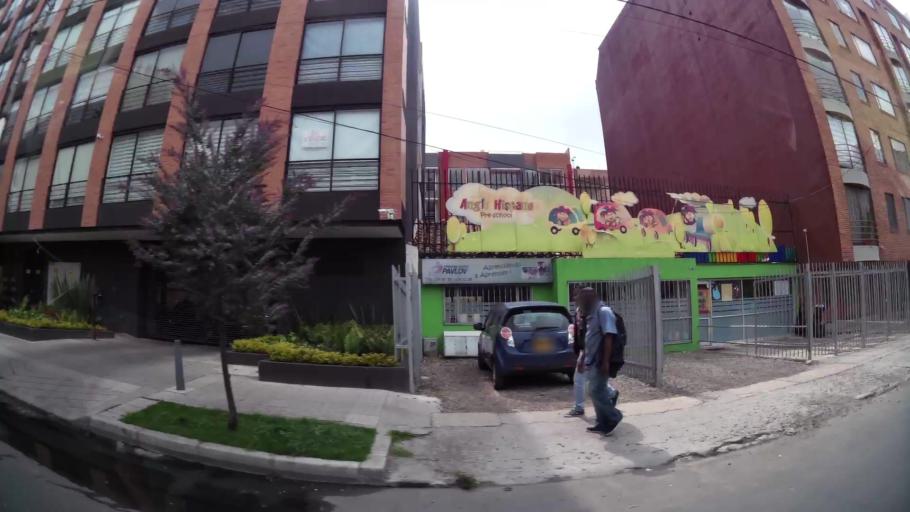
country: CO
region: Bogota D.C.
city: Barrio San Luis
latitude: 4.7249
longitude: -74.0415
